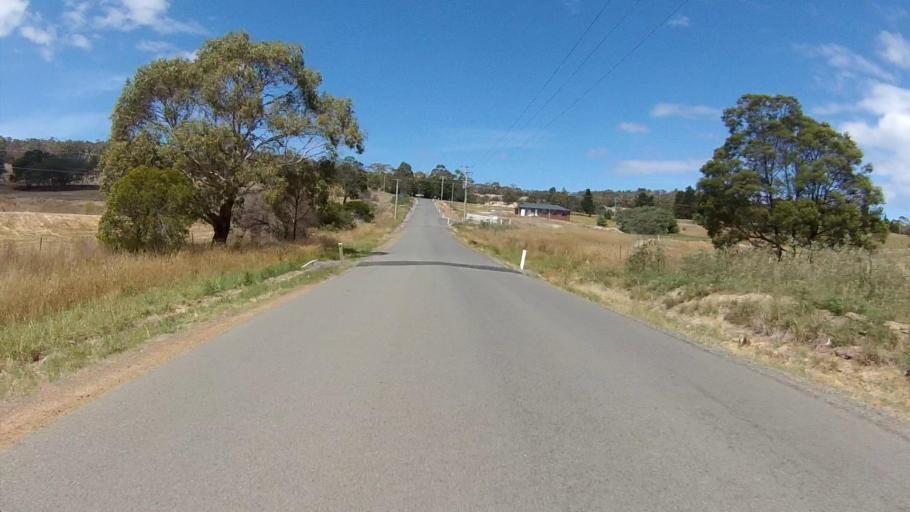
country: AU
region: Tasmania
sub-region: Sorell
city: Sorell
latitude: -42.8209
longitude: 147.6204
